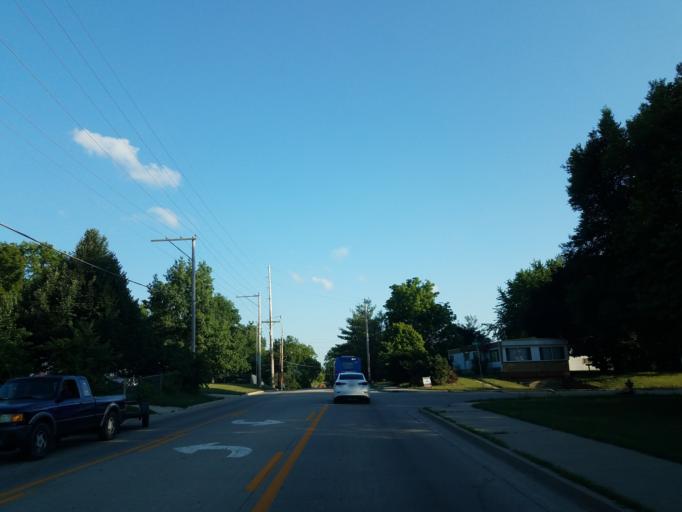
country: US
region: Illinois
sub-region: McLean County
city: Bloomington
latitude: 40.4749
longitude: -89.0163
